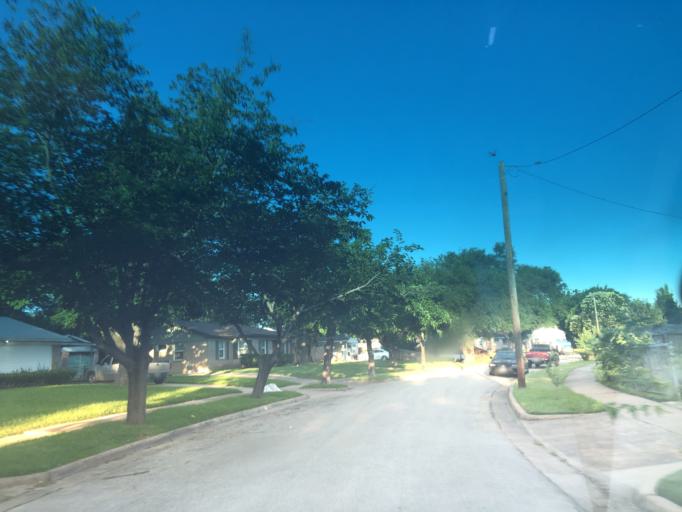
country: US
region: Texas
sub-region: Dallas County
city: Grand Prairie
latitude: 32.7075
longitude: -97.0140
